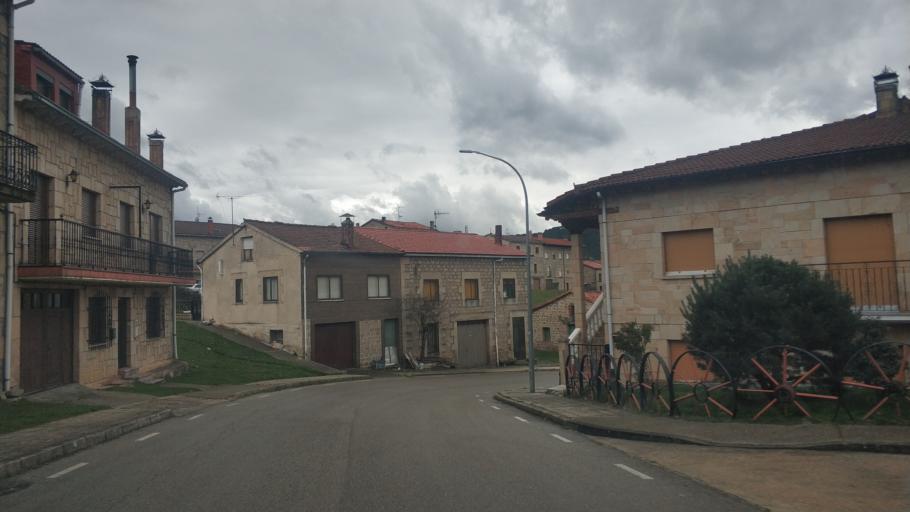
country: ES
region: Castille and Leon
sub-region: Provincia de Burgos
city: Canicosa de la Sierra
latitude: 41.9380
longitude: -3.0390
